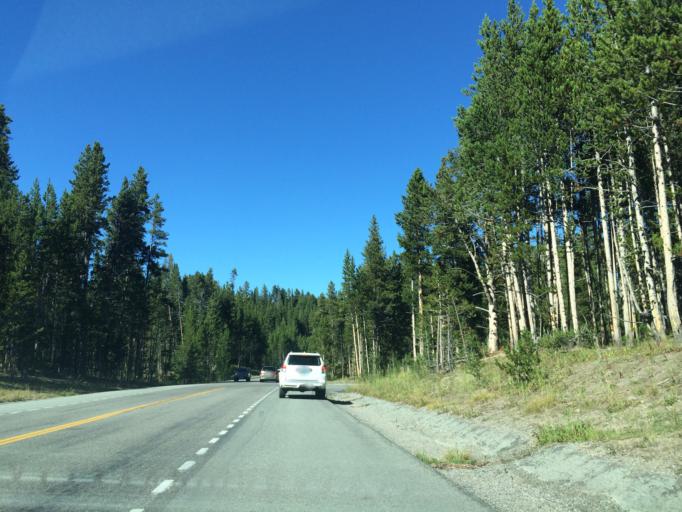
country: US
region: Montana
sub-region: Gallatin County
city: West Yellowstone
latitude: 44.7166
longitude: -110.5049
